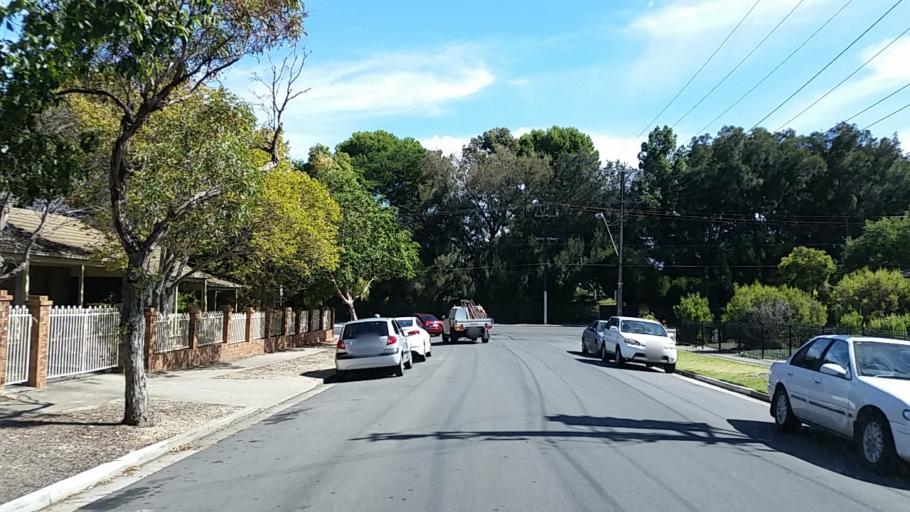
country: AU
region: South Australia
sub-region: Charles Sturt
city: Findon
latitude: -34.9259
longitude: 138.5321
